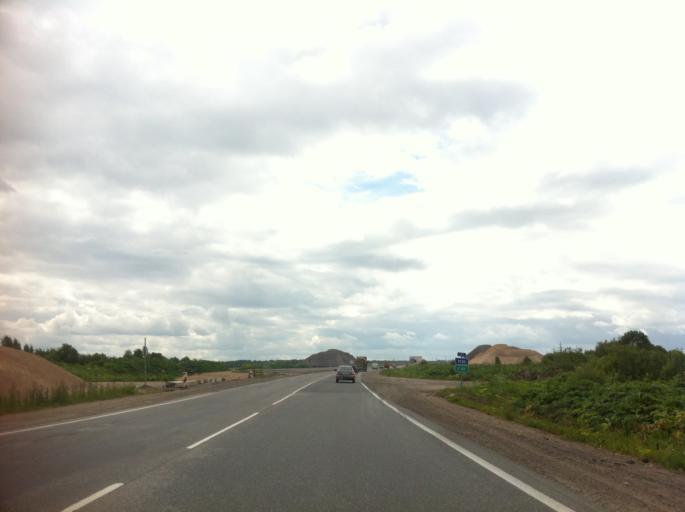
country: RU
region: Leningrad
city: Gatchina
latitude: 59.5445
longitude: 30.1639
